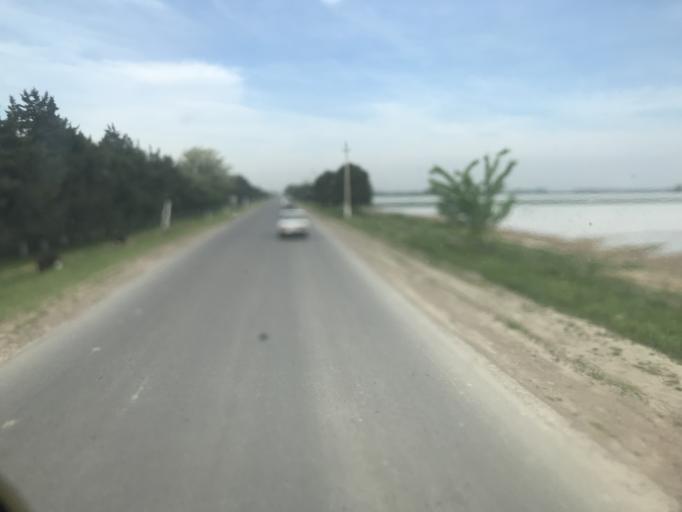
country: KZ
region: Ongtustik Qazaqstan
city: Asykata
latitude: 40.9845
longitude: 68.2952
